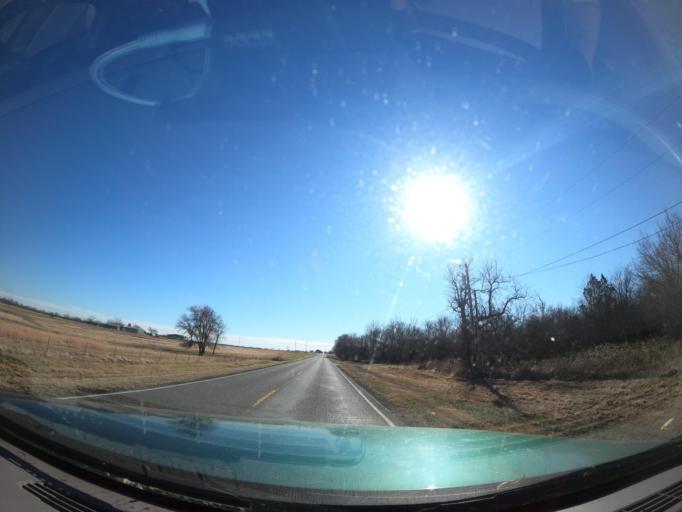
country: US
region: Oklahoma
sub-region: Muskogee County
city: Haskell
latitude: 35.6777
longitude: -95.6422
